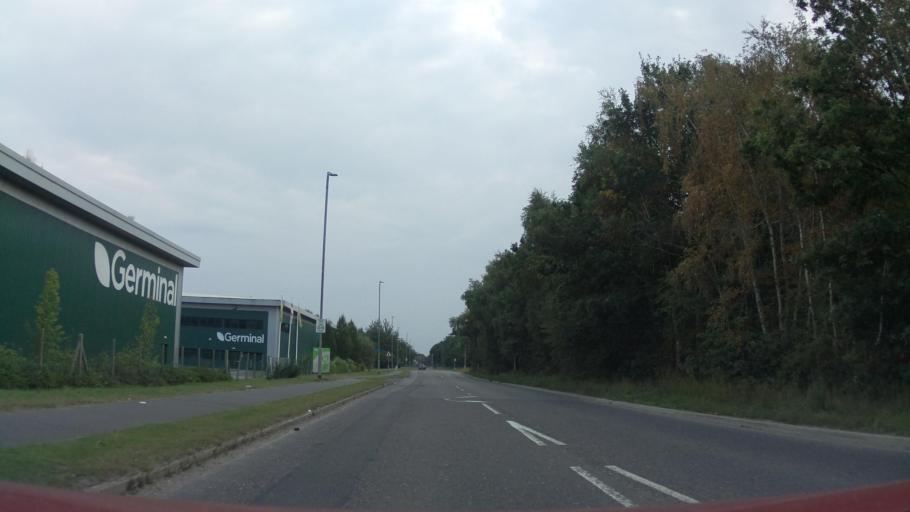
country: GB
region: England
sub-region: Lincolnshire
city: Skellingthorpe
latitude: 53.1526
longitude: -0.6707
